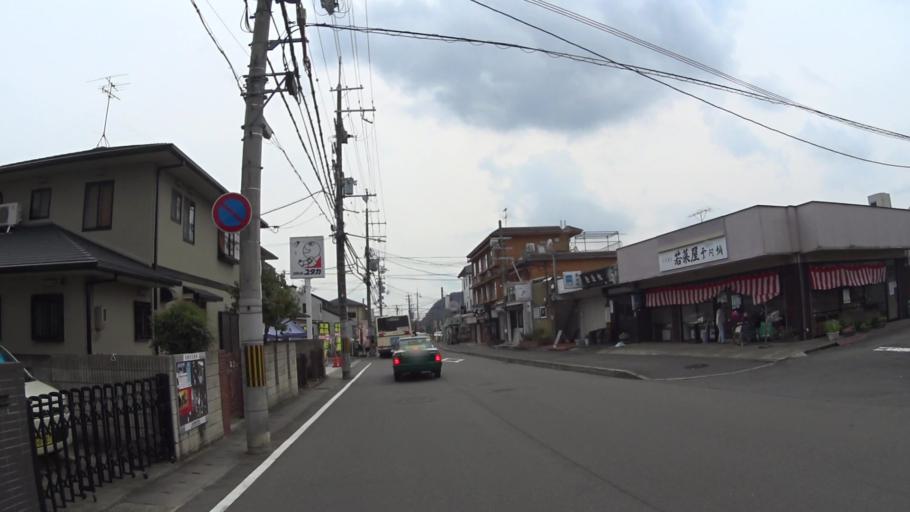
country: JP
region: Kyoto
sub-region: Kyoto-shi
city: Kamigyo-ku
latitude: 35.0669
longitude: 135.7930
